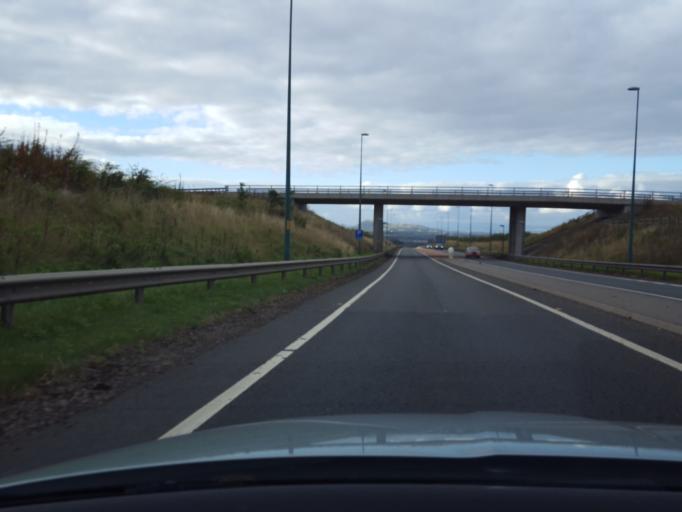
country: GB
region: Scotland
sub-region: Fife
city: Pathhead
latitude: 55.8935
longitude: -3.0017
